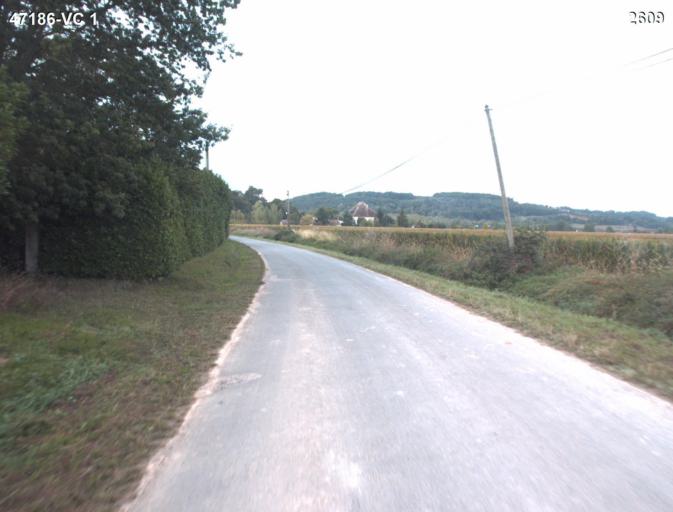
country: FR
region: Aquitaine
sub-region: Departement du Lot-et-Garonne
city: Port-Sainte-Marie
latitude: 44.2104
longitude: 0.4397
